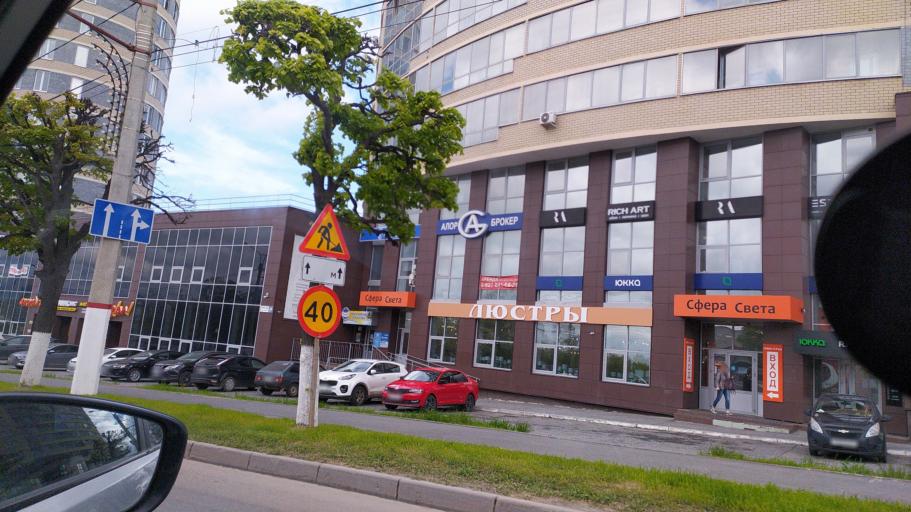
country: RU
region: Chuvashia
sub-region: Cheboksarskiy Rayon
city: Cheboksary
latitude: 56.1402
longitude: 47.2675
